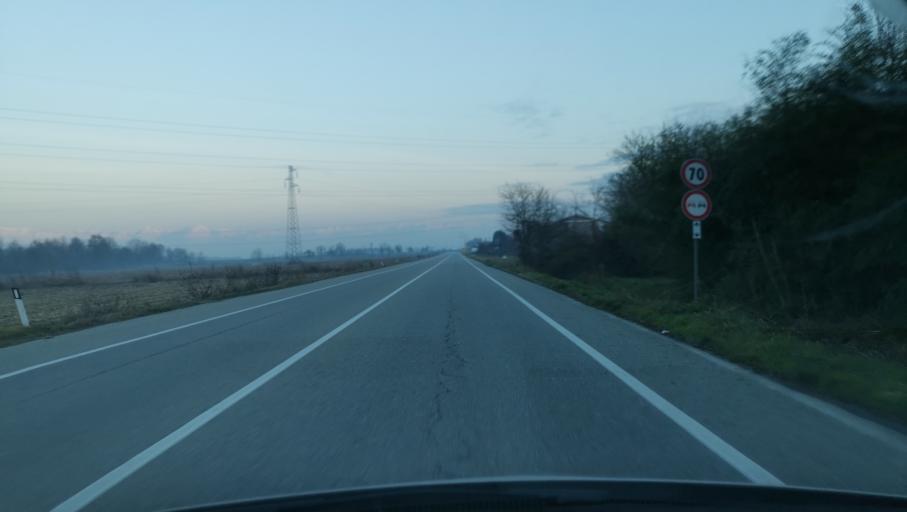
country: IT
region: Piedmont
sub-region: Provincia di Torino
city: Chivasso
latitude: 45.2218
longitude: 7.8906
